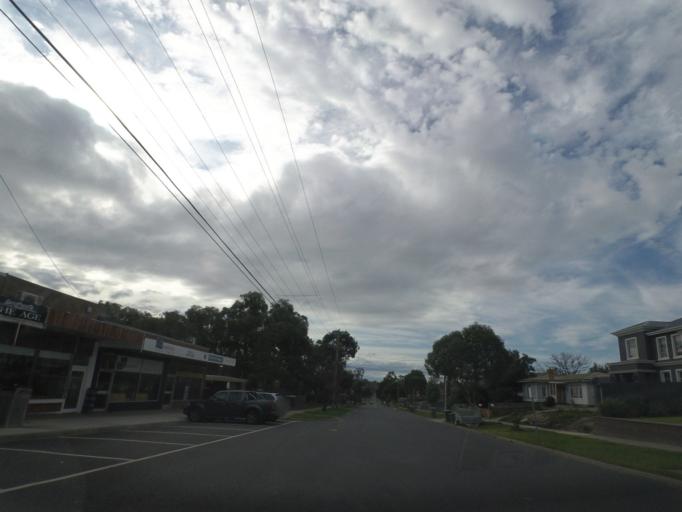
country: AU
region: Victoria
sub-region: Maroondah
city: Heathmont
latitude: -37.8289
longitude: 145.2373
